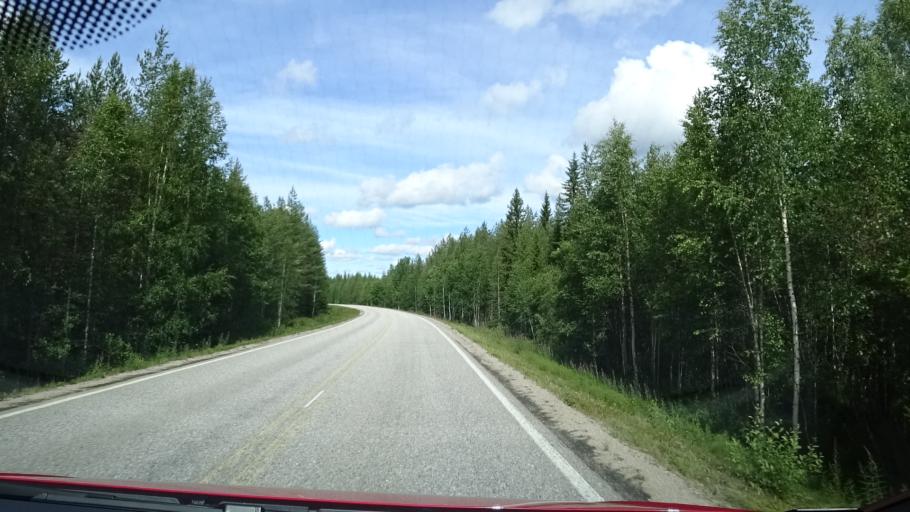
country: FI
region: Kainuu
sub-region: Kehys-Kainuu
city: Kuhmo
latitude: 64.4492
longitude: 29.7853
